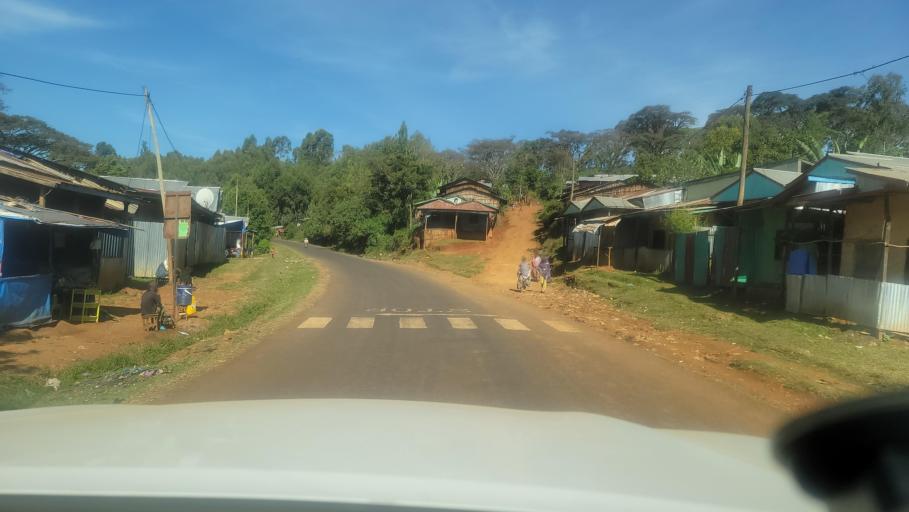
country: ET
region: Oromiya
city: Agaro
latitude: 7.7990
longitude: 36.4769
